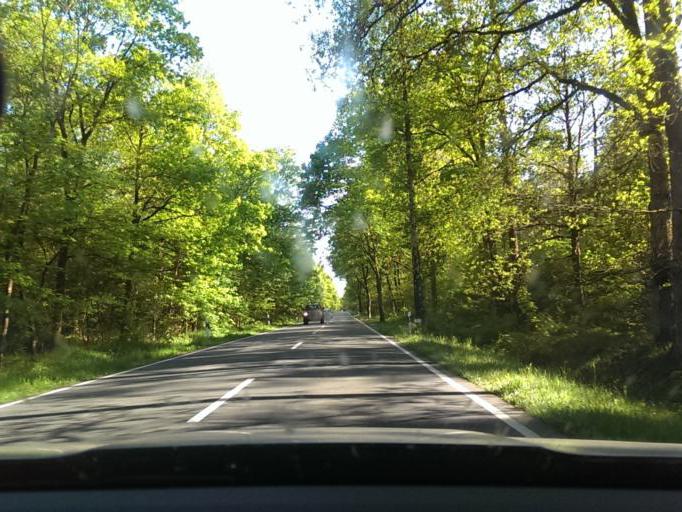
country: DE
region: Lower Saxony
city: Hambuhren
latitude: 52.6270
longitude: 9.9298
